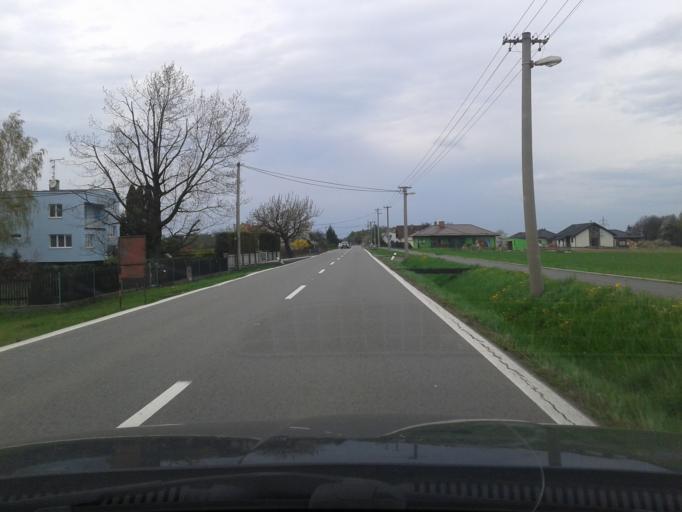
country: CZ
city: Sedliste
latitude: 49.7251
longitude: 18.3668
